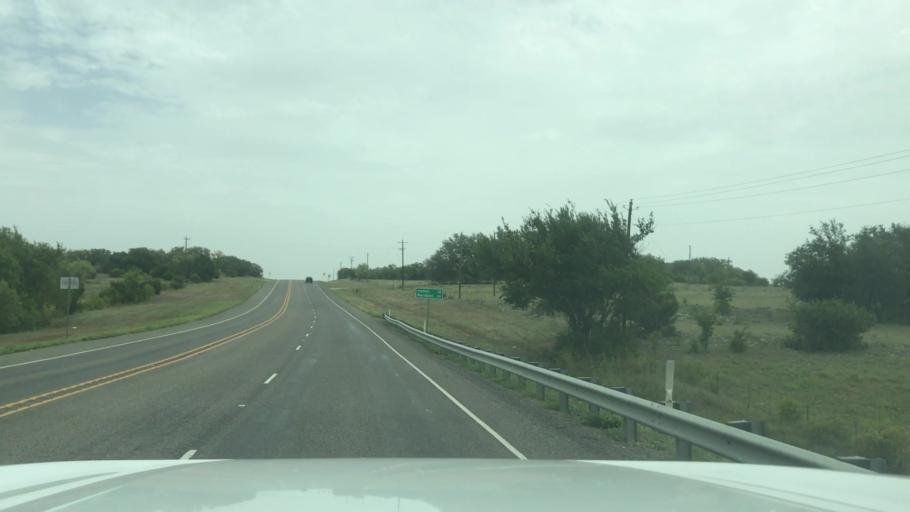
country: US
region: Texas
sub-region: Hamilton County
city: Hico
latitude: 31.9806
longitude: -98.0201
